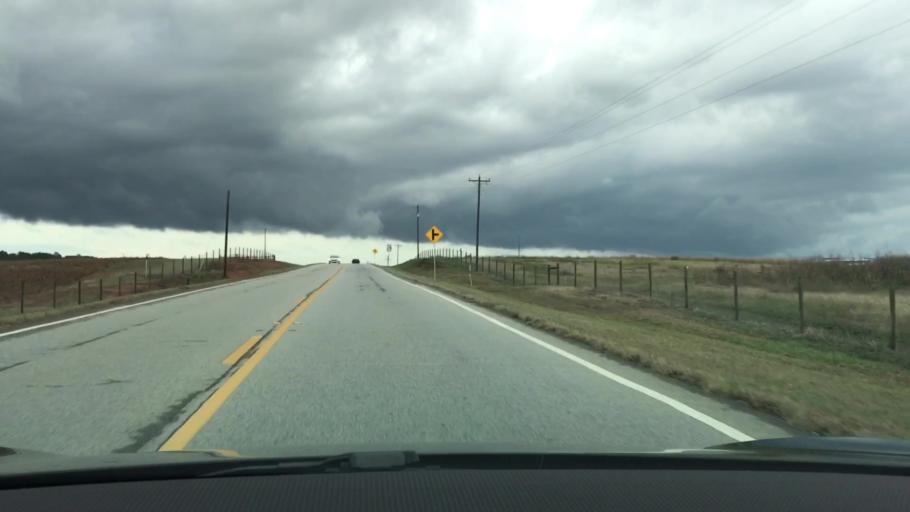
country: US
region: Georgia
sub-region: Oconee County
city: Watkinsville
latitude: 33.7289
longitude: -83.3026
